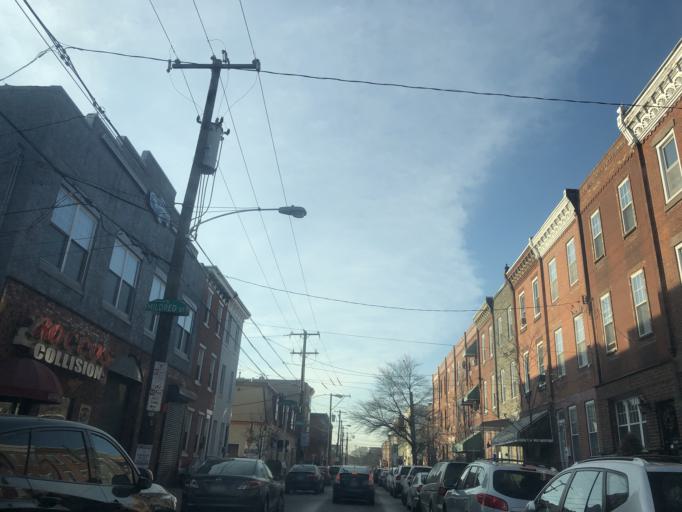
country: US
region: Pennsylvania
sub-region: Philadelphia County
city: Philadelphia
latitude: 39.9317
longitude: -75.1581
